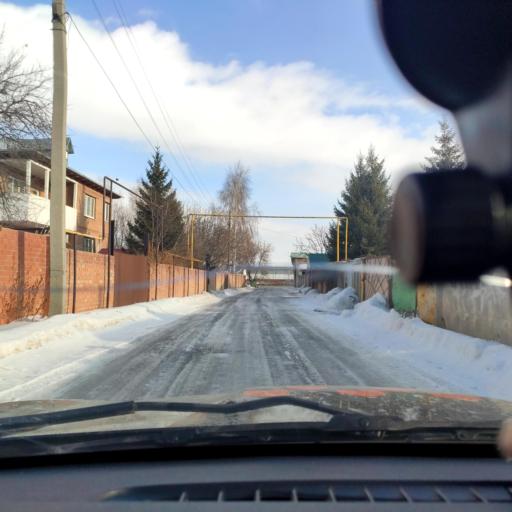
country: RU
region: Samara
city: Tol'yatti
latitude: 53.5751
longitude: 49.3211
